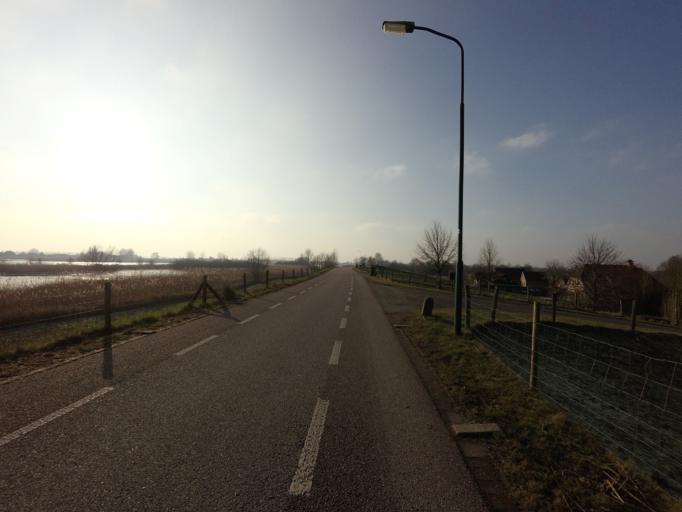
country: NL
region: South Holland
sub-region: Gemeente Schoonhoven
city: Schoonhoven
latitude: 51.9424
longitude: 4.8928
